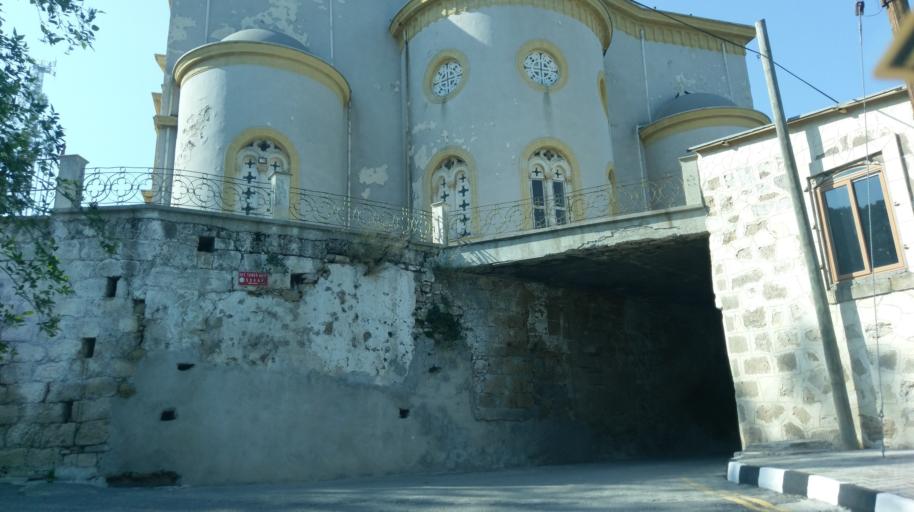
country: CY
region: Ammochostos
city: Lefkonoiko
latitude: 35.3723
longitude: 33.7541
